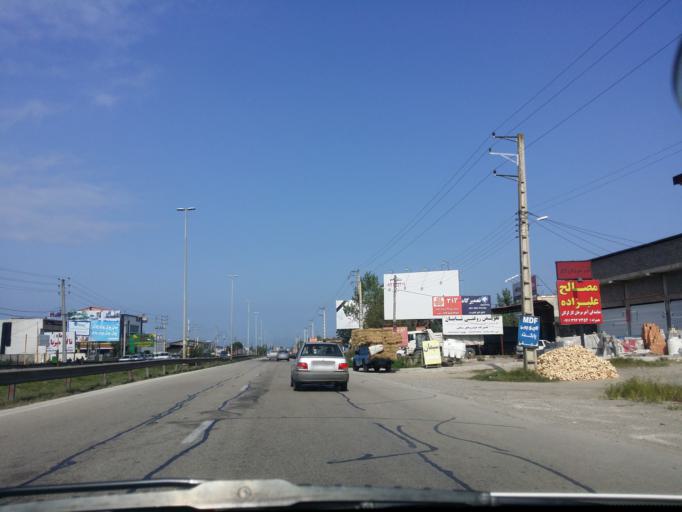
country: IR
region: Mazandaran
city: Chalus
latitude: 36.6637
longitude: 51.3983
